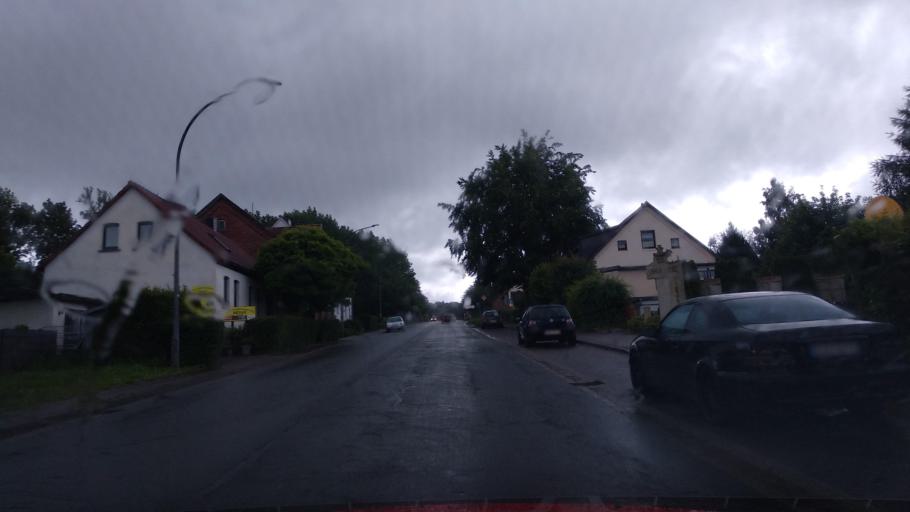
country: DE
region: Lower Saxony
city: Obernkirchen
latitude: 52.2617
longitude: 9.1350
